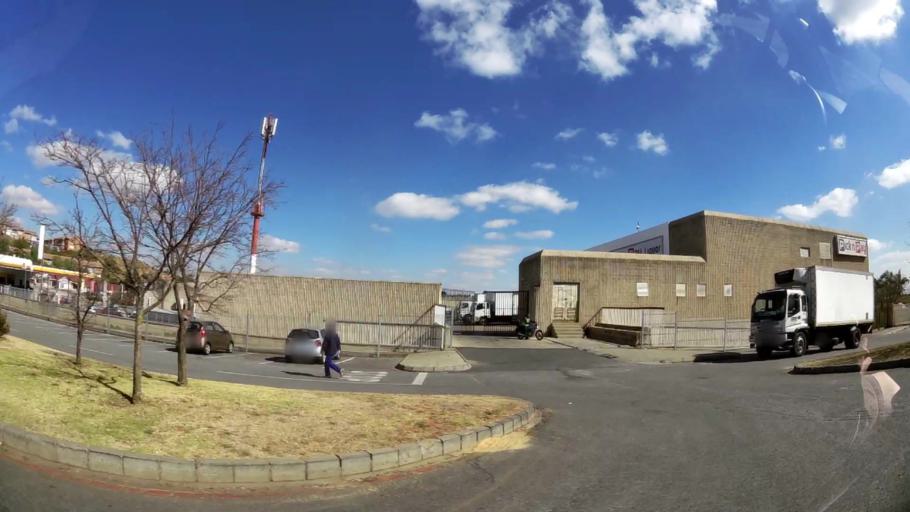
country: ZA
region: Gauteng
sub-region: West Rand District Municipality
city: Krugersdorp
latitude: -26.0962
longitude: 27.8035
